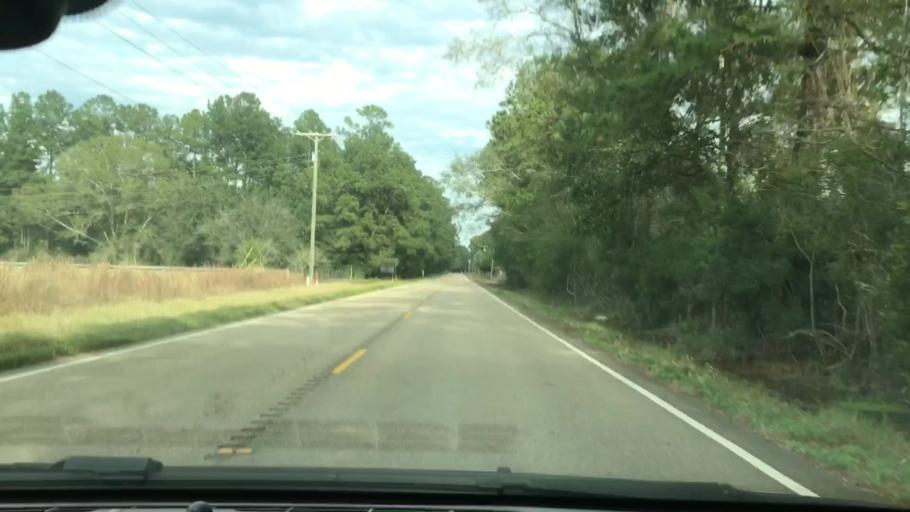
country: US
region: Louisiana
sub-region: Saint Tammany Parish
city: Abita Springs
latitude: 30.4997
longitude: -89.9971
